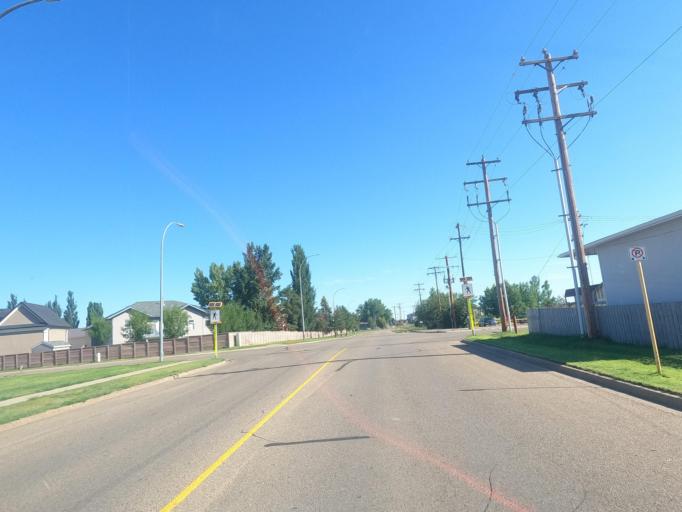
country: CA
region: Alberta
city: Brooks
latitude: 50.5791
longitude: -111.9001
